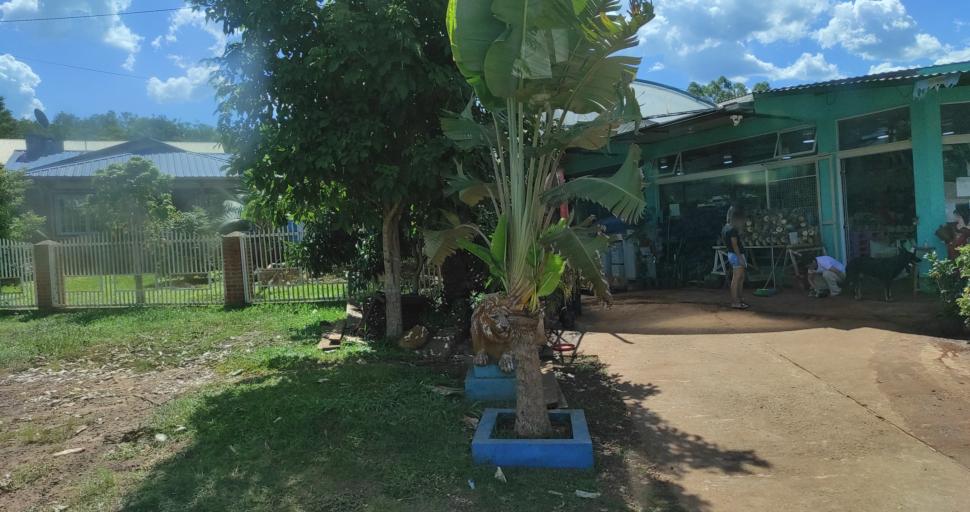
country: AR
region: Misiones
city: El Soberbio
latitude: -27.2839
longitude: -54.1975
